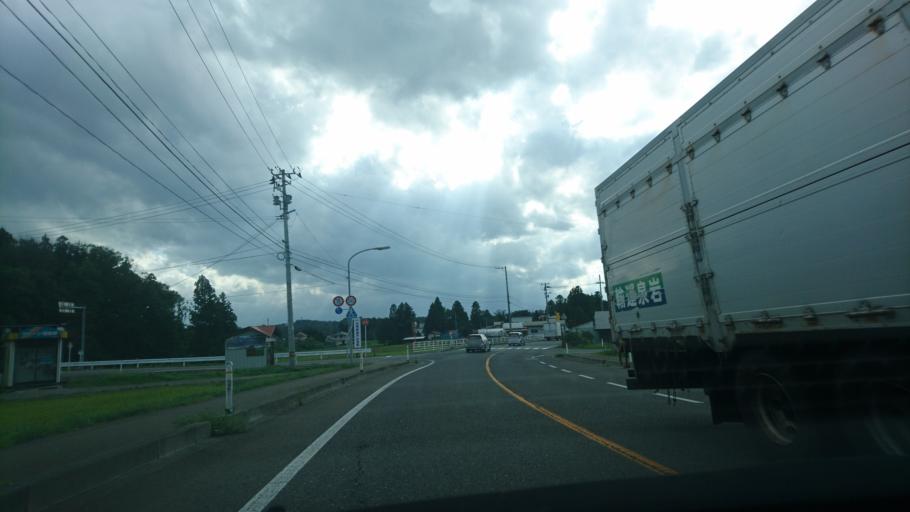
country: JP
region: Iwate
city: Hanamaki
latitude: 39.3930
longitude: 141.1639
